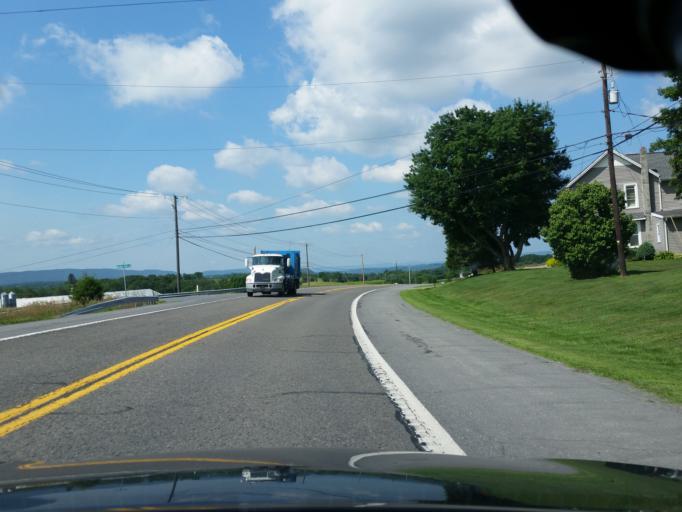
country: US
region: Pennsylvania
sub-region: Dauphin County
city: Matamoras
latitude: 40.4796
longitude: -76.9055
